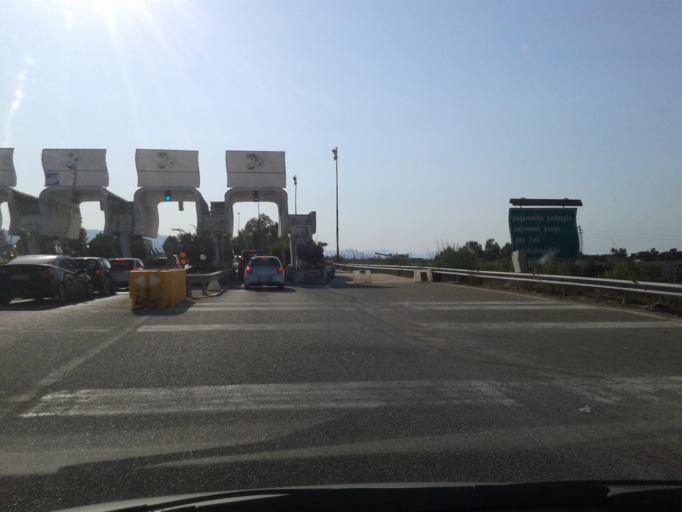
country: IT
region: Sicily
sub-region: Palermo
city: Campofelice di Roccella
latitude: 37.9800
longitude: 13.8454
